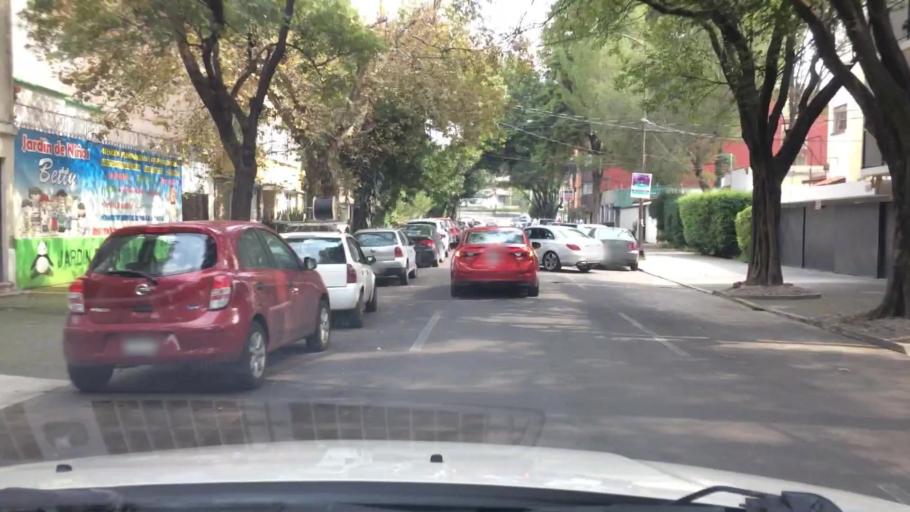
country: MX
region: Mexico City
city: Benito Juarez
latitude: 19.4029
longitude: -99.1656
